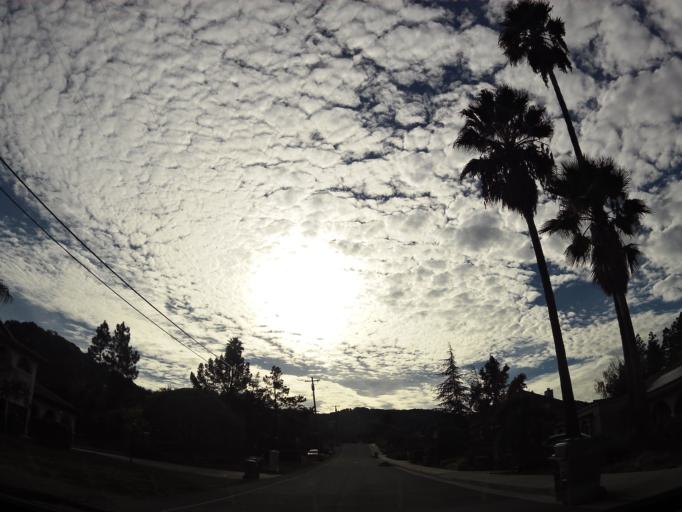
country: US
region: California
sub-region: Santa Clara County
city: Seven Trees
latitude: 37.1964
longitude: -121.8347
